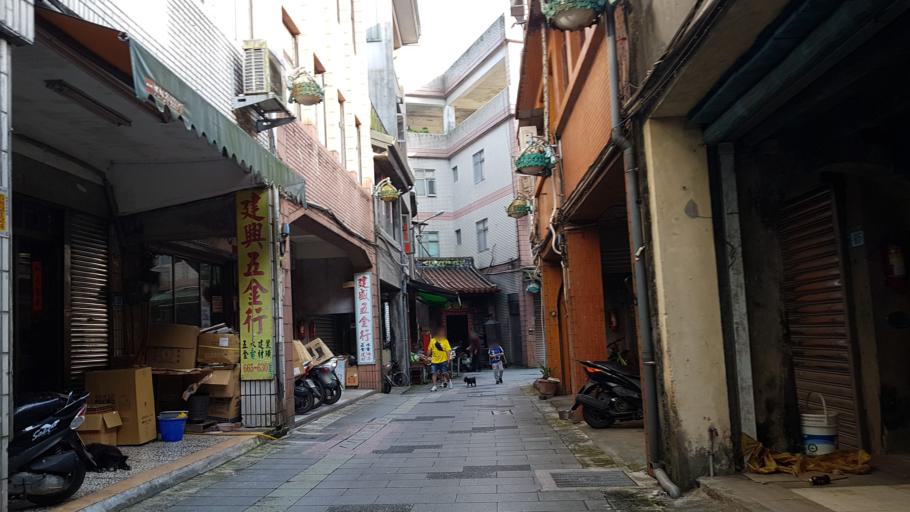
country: TW
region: Taiwan
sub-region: Yilan
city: Yilan
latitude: 24.9366
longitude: 121.7120
